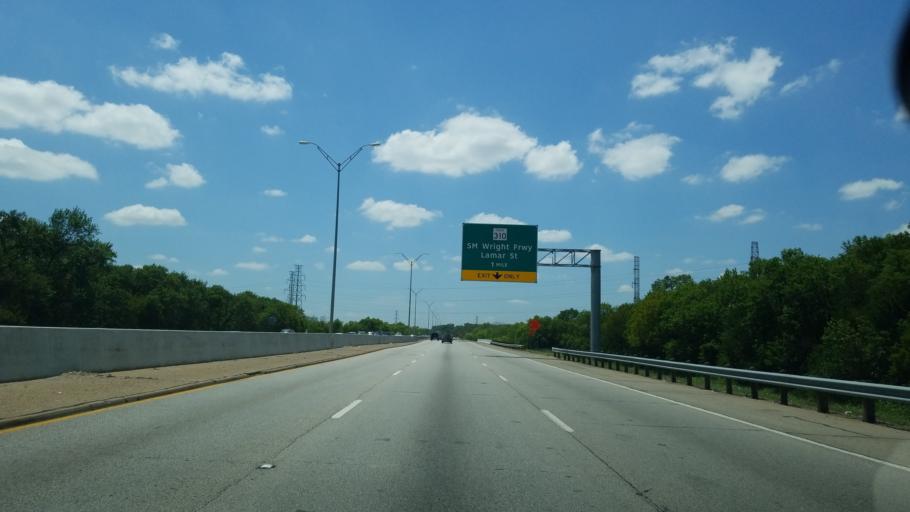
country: US
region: Texas
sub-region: Dallas County
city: Dallas
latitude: 32.7461
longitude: -96.7335
